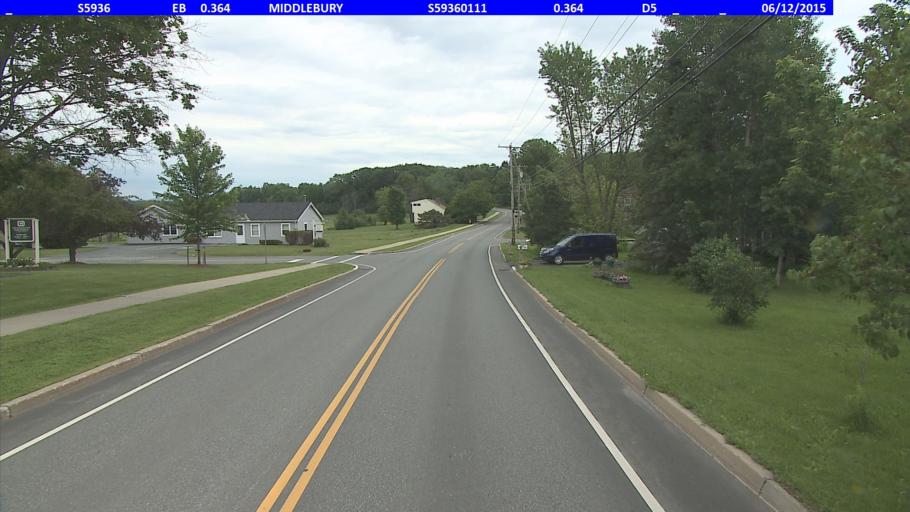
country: US
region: Vermont
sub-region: Addison County
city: Middlebury (village)
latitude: 44.0205
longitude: -73.1561
